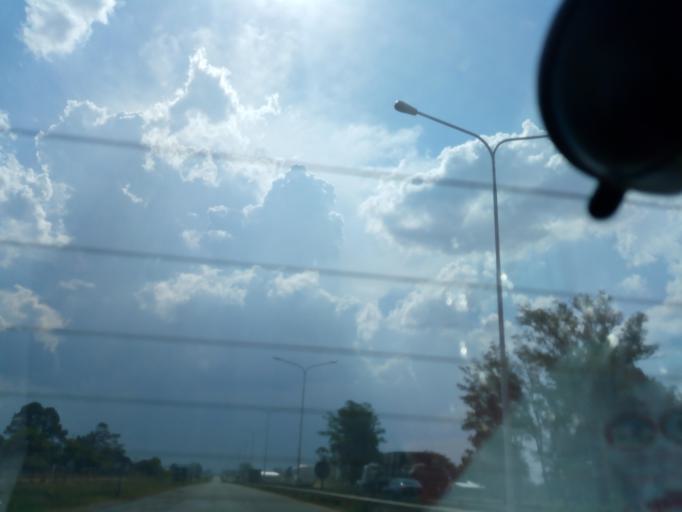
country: AR
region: Corrientes
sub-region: Departamento de Paso de los Libres
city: Paso de los Libres
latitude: -29.7220
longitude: -57.1519
